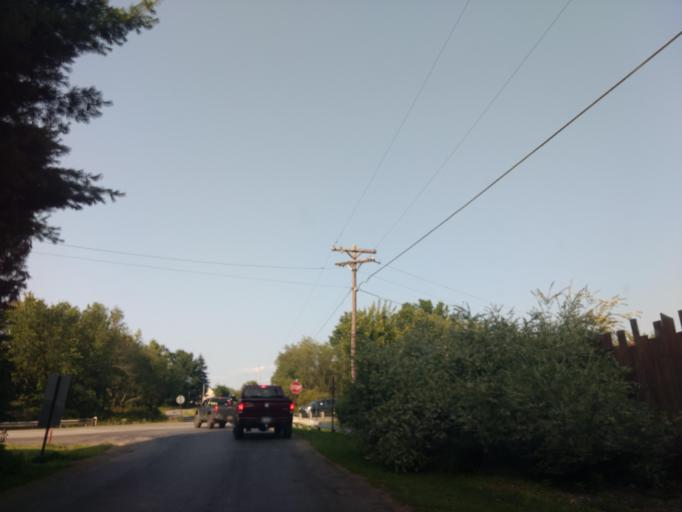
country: US
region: Pennsylvania
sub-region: Lawrence County
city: Ellport
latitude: 40.9691
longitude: -80.2159
